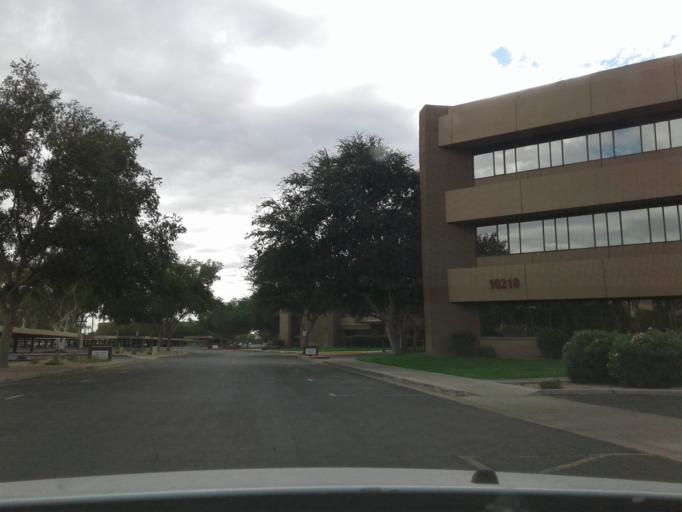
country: US
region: Arizona
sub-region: Maricopa County
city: Glendale
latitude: 33.5787
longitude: -112.1145
